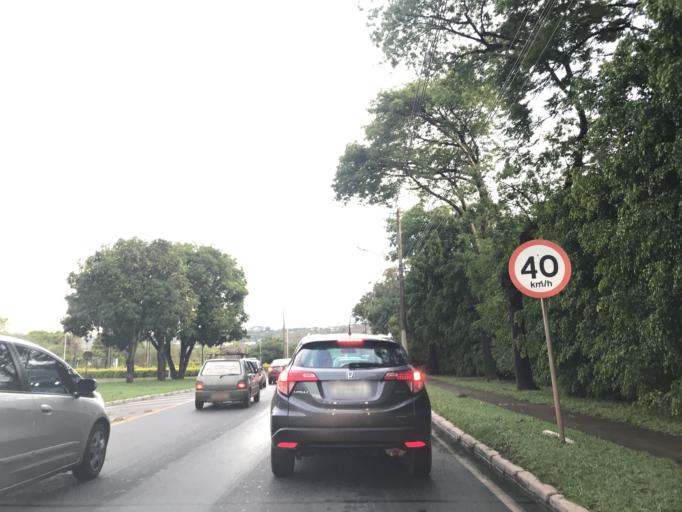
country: BR
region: Federal District
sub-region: Brasilia
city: Brasilia
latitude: -15.8542
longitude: -47.8777
